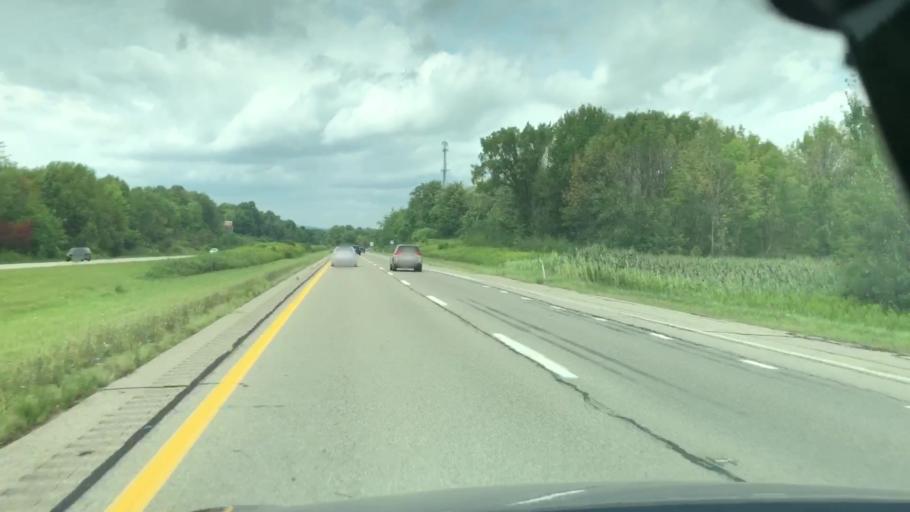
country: US
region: Pennsylvania
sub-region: Crawford County
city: Meadville
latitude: 41.7206
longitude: -80.2025
